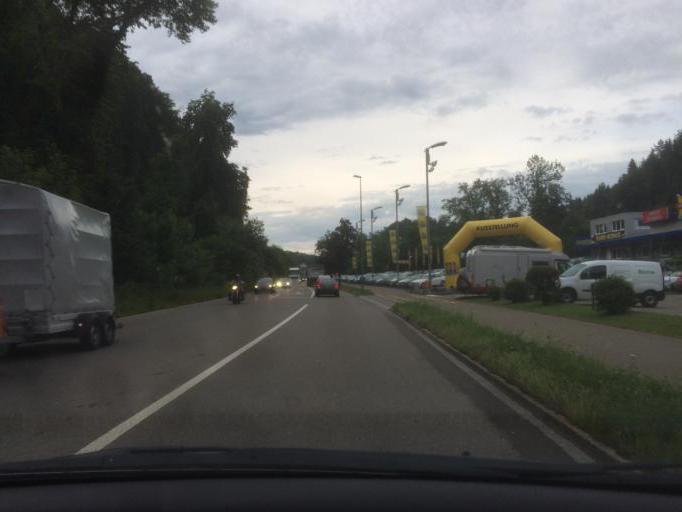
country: CH
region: Zurich
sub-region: Bezirk Hinwil
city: Wetzikon / Robenhausen
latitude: 47.3386
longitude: 8.7629
